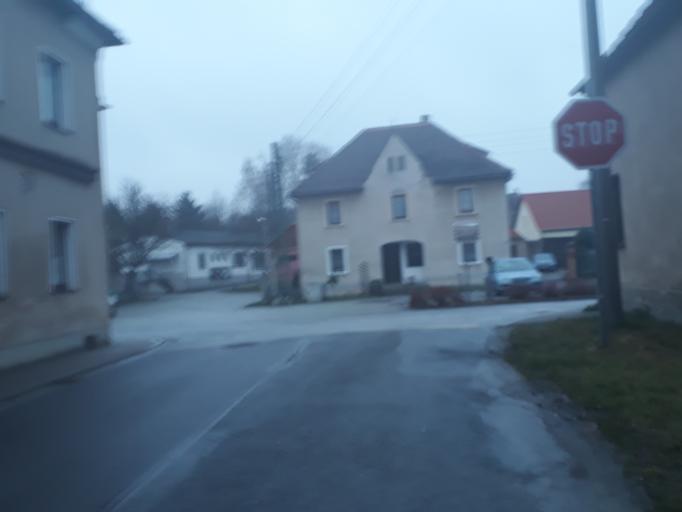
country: DE
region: Saxony
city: Guttau
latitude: 51.2596
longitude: 14.5596
